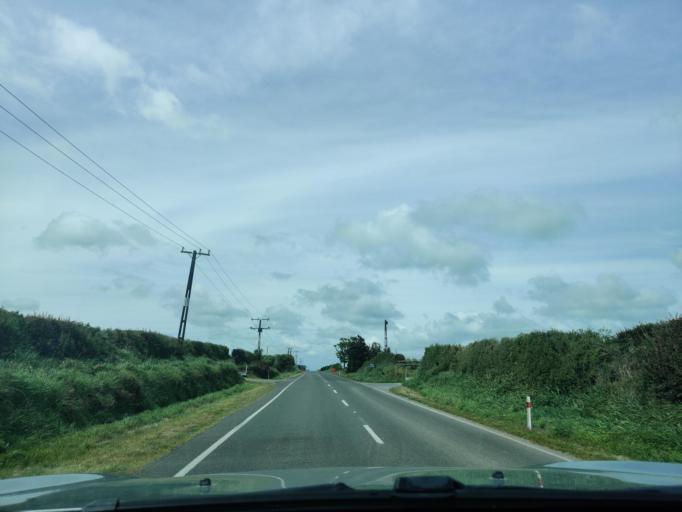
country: NZ
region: Taranaki
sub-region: South Taranaki District
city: Eltham
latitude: -39.4278
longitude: 174.1657
